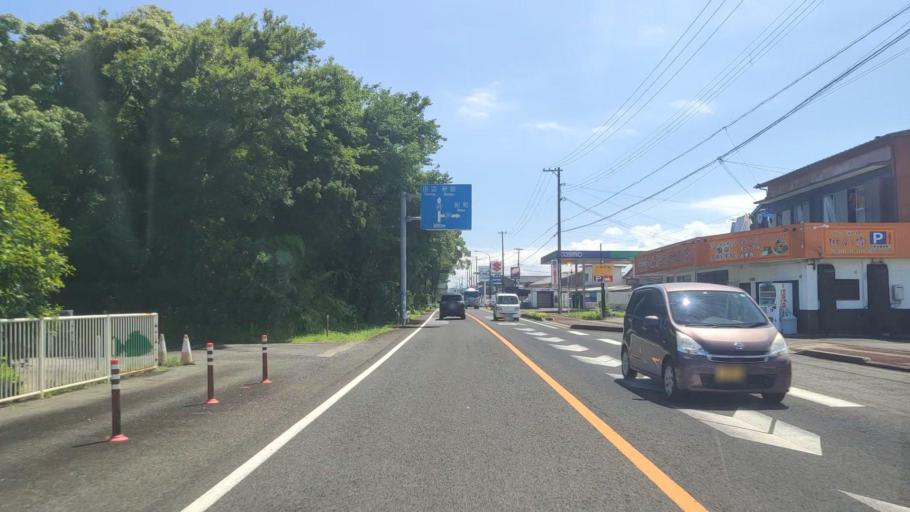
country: JP
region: Wakayama
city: Shingu
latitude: 33.8718
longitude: 136.0853
